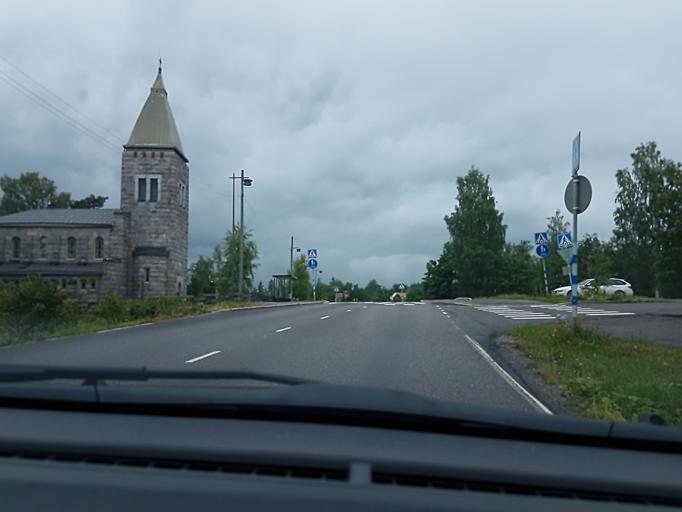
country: FI
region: Uusimaa
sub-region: Helsinki
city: Pornainen
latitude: 60.4738
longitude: 25.3770
